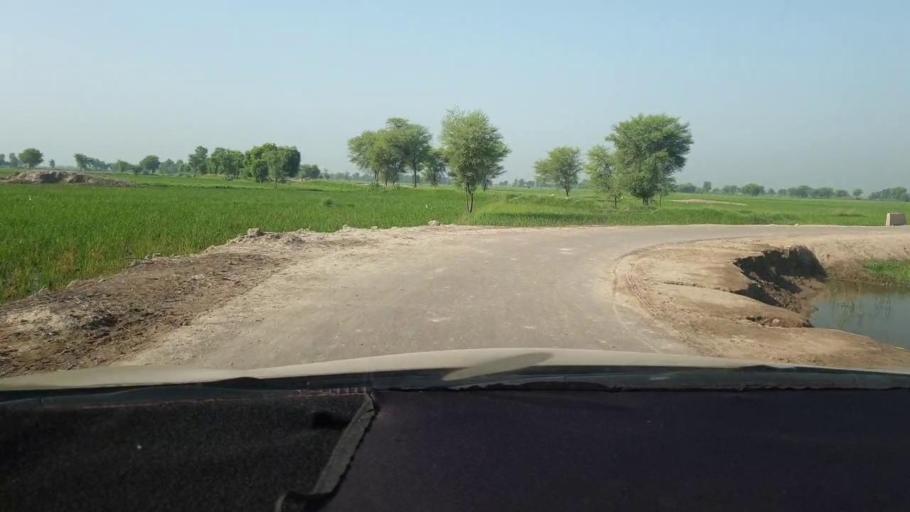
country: PK
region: Sindh
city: Miro Khan
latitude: 27.7529
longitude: 68.1569
